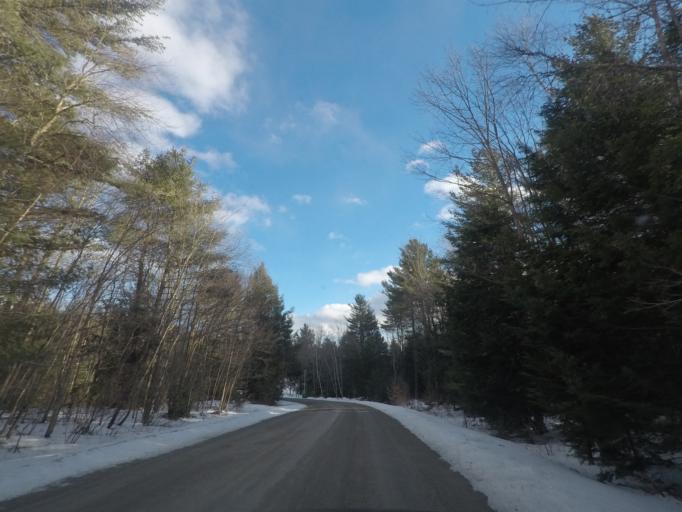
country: US
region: New York
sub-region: Rensselaer County
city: Poestenkill
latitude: 42.7441
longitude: -73.4779
